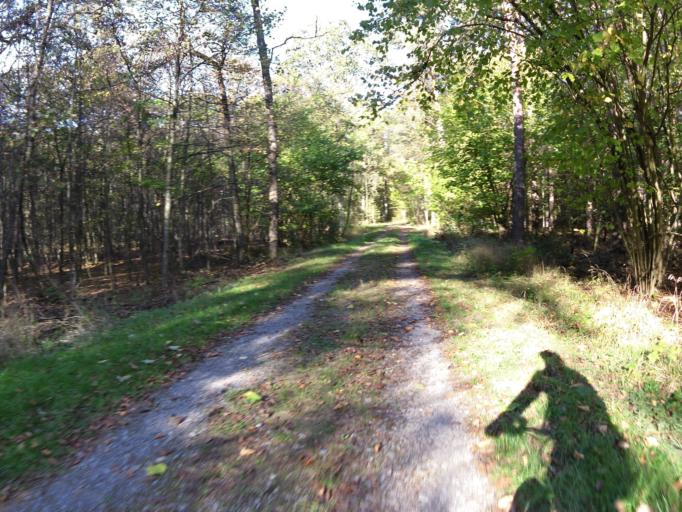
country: DE
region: Bavaria
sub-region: Regierungsbezirk Unterfranken
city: Sulzfeld am Main
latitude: 49.7178
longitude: 10.0895
